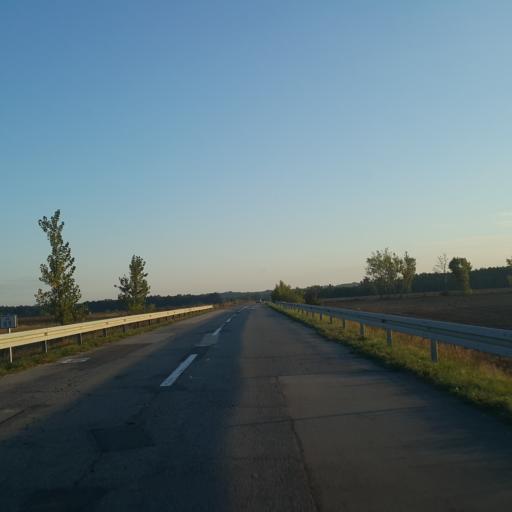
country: RS
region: Central Serbia
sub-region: Borski Okrug
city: Negotin
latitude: 44.1381
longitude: 22.3481
